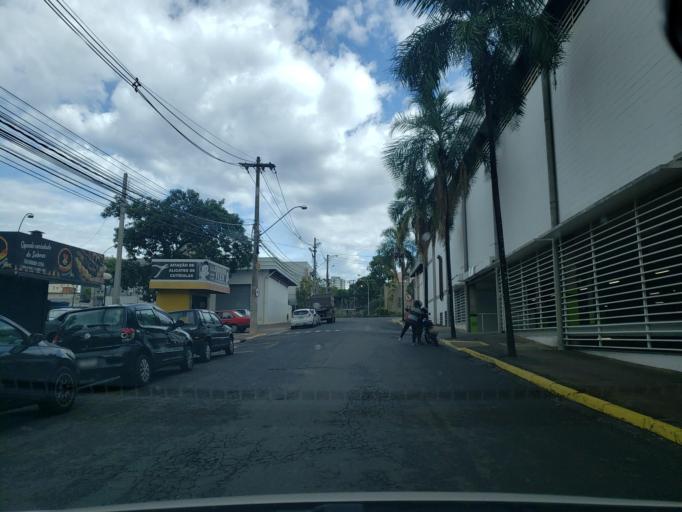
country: BR
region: Sao Paulo
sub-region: Bauru
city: Bauru
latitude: -22.3398
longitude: -49.0447
